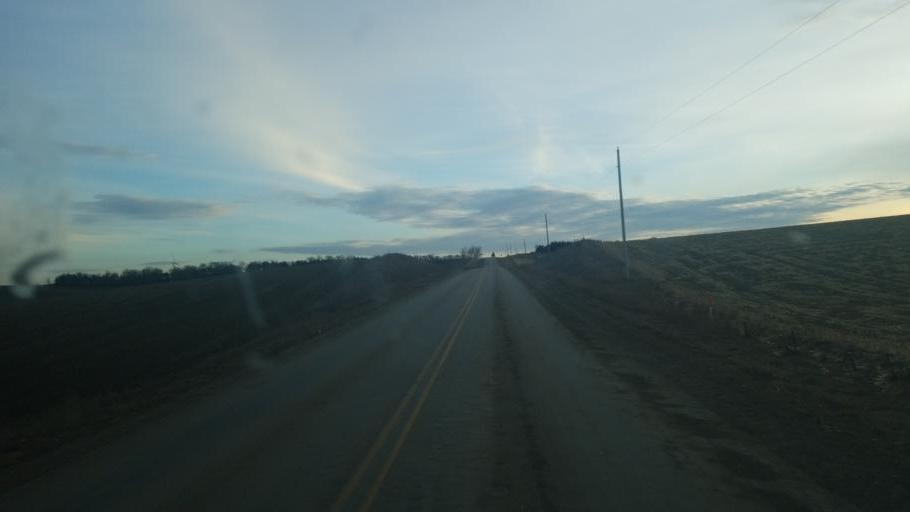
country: US
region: Nebraska
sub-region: Knox County
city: Bloomfield
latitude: 42.7092
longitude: -97.6627
